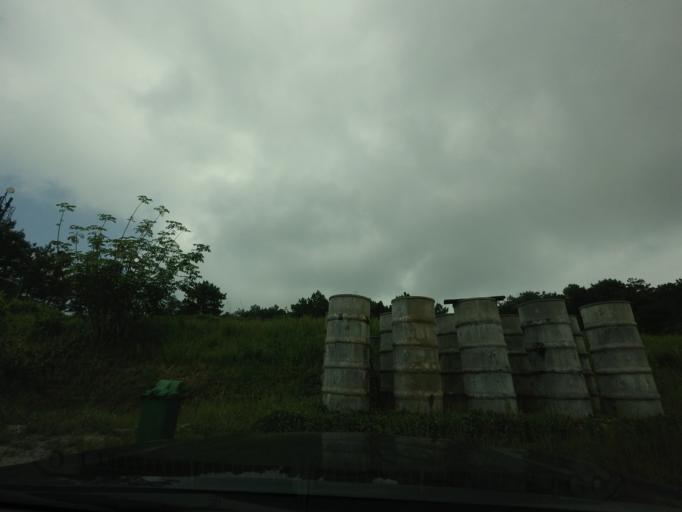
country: TH
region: Loei
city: Phu Ruea
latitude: 17.5078
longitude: 101.3452
